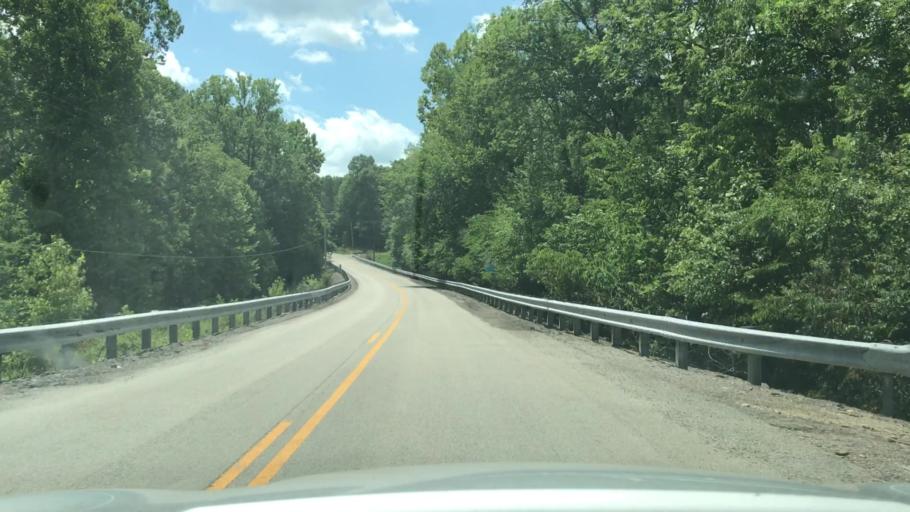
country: US
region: Kentucky
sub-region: Hopkins County
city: Nortonville
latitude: 37.1218
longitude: -87.3202
